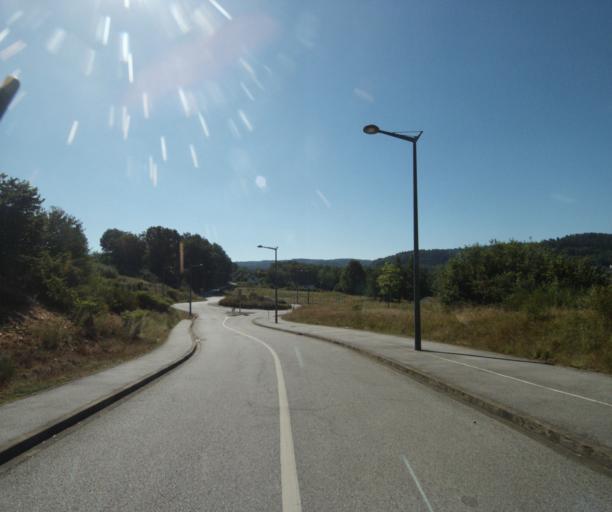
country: FR
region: Lorraine
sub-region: Departement des Vosges
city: Chantraine
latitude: 48.1521
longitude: 6.4621
